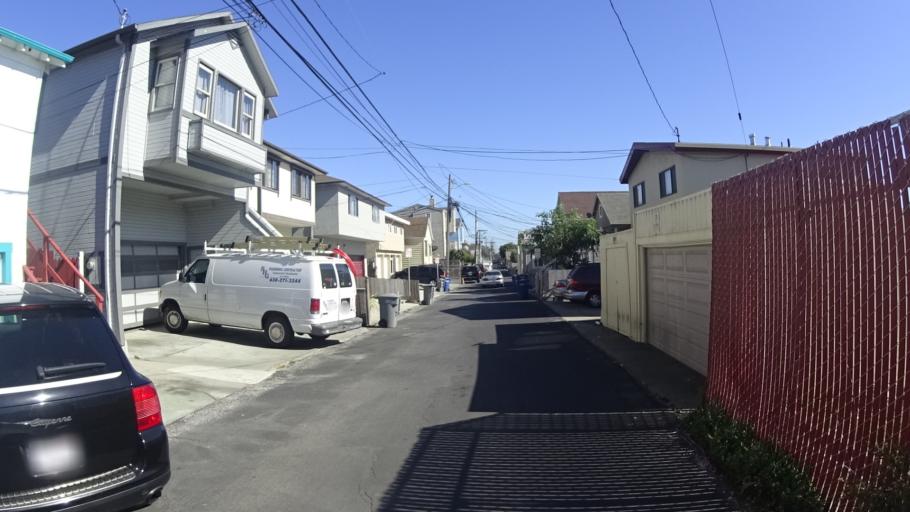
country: US
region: California
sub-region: San Mateo County
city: South San Francisco
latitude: 37.6554
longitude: -122.4183
